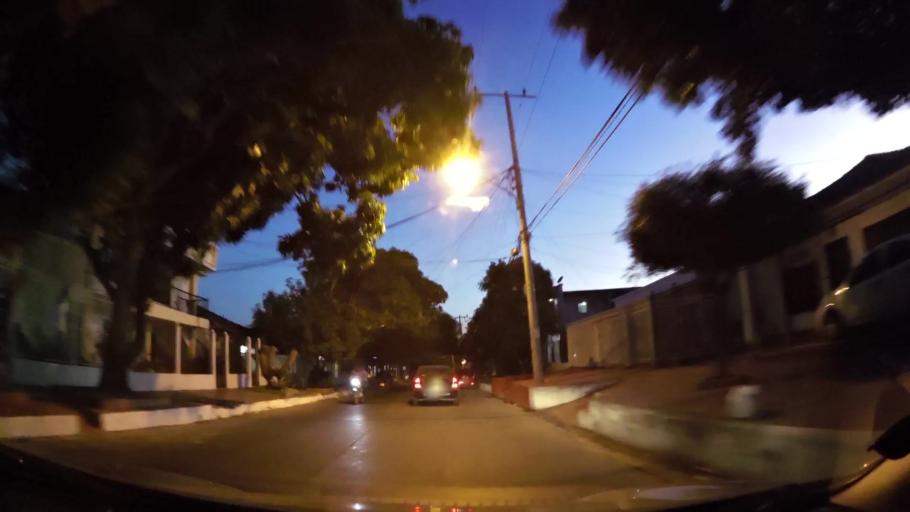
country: CO
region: Atlantico
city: Barranquilla
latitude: 10.9706
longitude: -74.8036
